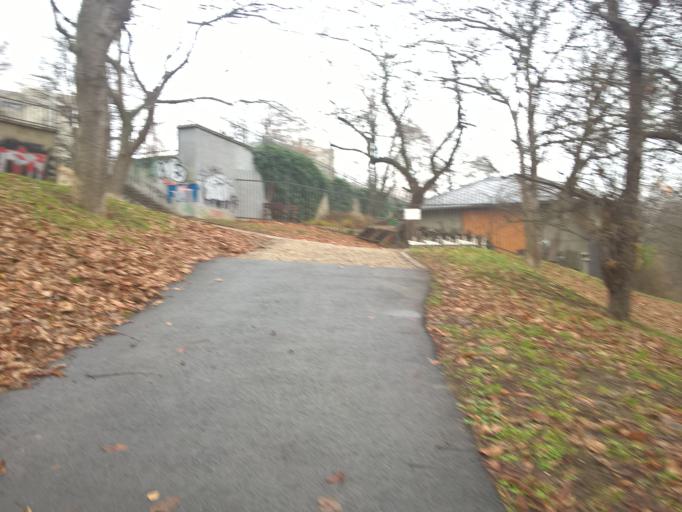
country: CZ
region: Praha
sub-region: Praha 1
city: Mala Strana
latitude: 50.0787
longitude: 14.3947
